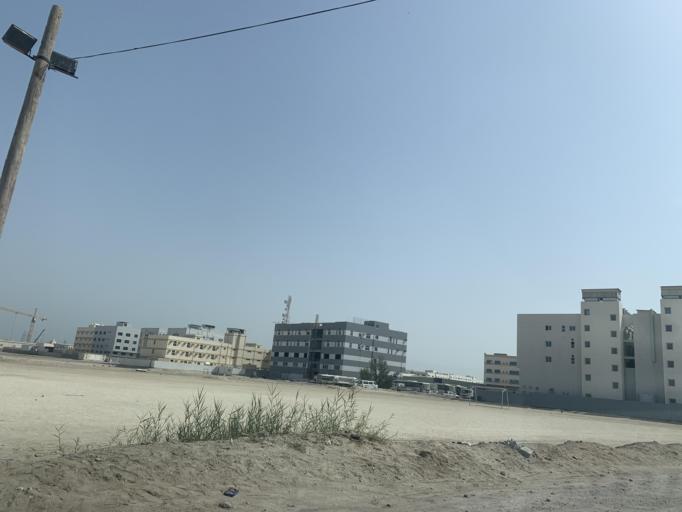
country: BH
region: Northern
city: Madinat `Isa
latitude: 26.1887
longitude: 50.5492
